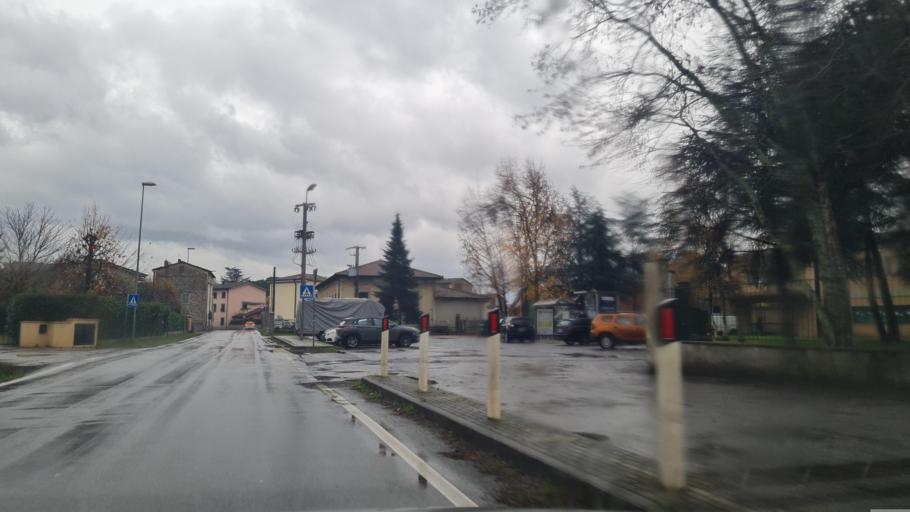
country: IT
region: Tuscany
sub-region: Provincia di Lucca
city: Lucca
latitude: 43.8625
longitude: 10.4809
